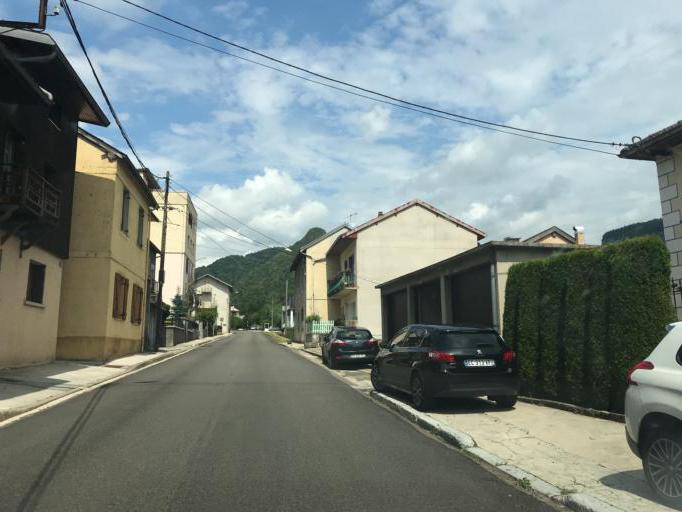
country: FR
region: Franche-Comte
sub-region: Departement du Jura
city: Saint-Claude
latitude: 46.4002
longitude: 5.8634
